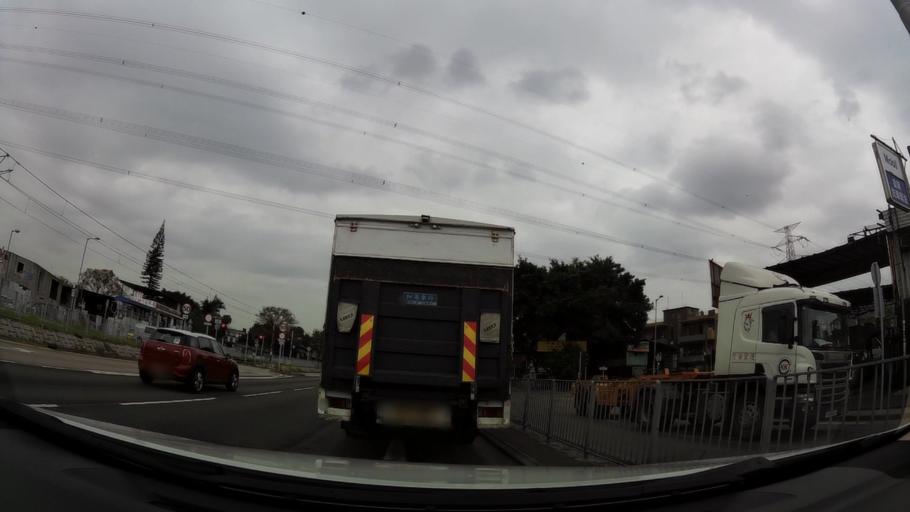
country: HK
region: Tuen Mun
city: Tuen Mun
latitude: 22.4262
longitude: 113.9890
